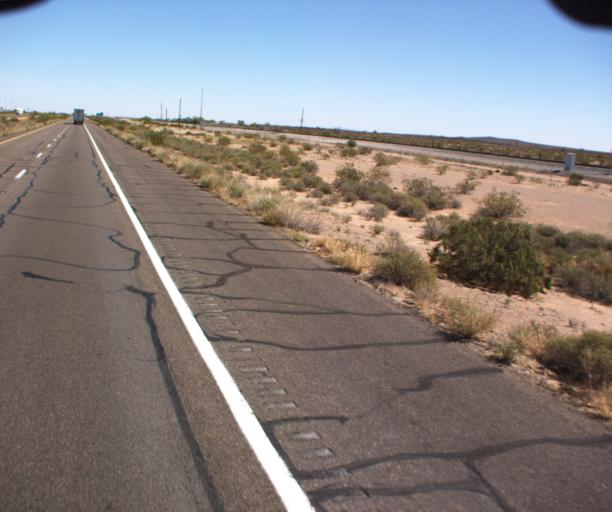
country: US
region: Arizona
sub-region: Maricopa County
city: Gila Bend
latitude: 32.8570
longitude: -113.2255
